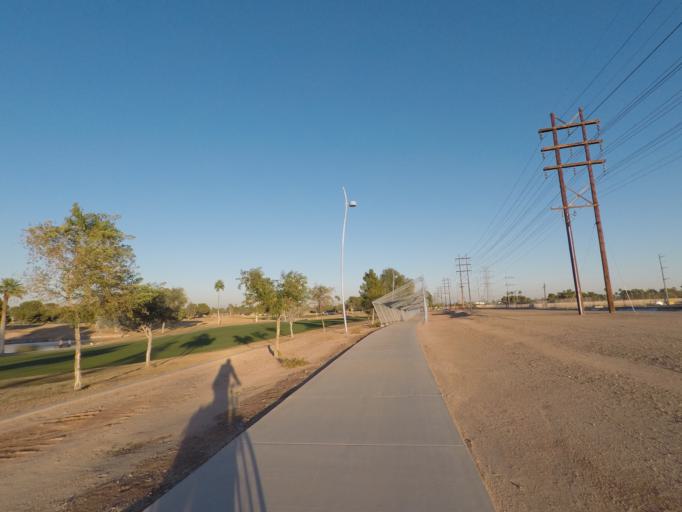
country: US
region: Arizona
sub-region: Maricopa County
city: Guadalupe
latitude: 33.3570
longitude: -111.9366
